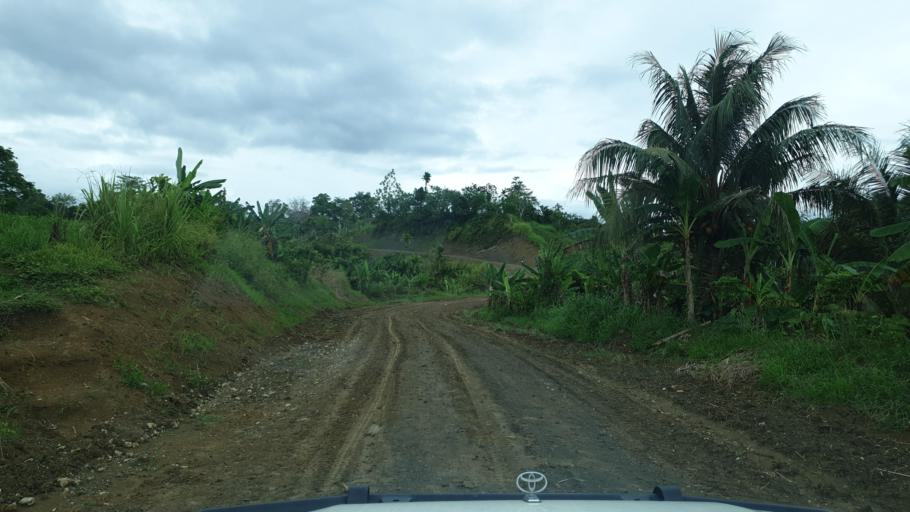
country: PG
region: Gulf
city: Kerema
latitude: -7.9874
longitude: 145.8325
